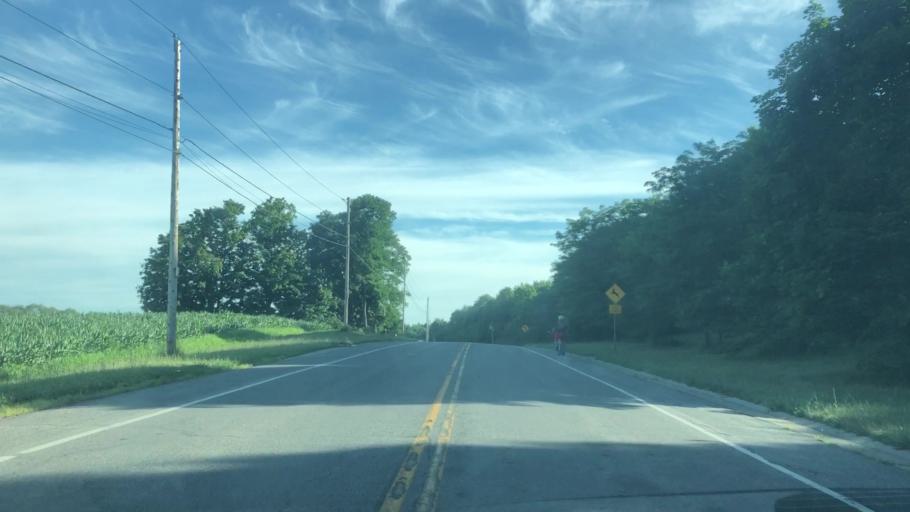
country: US
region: New York
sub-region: Ontario County
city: Victor
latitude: 43.0428
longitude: -77.3980
